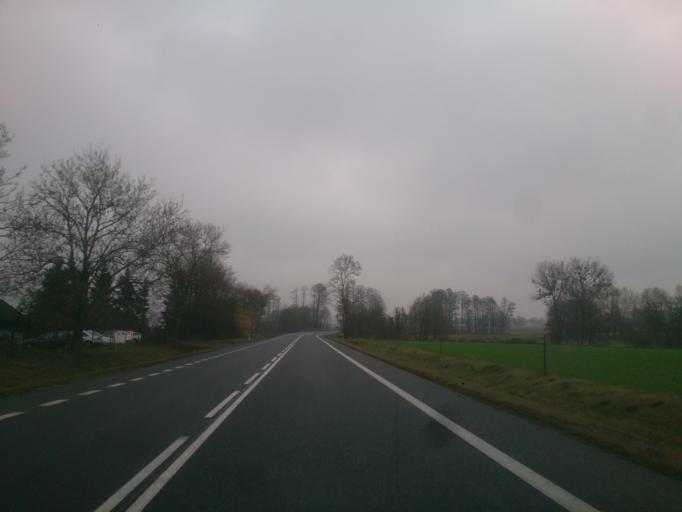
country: PL
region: Masovian Voivodeship
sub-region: Powiat sierpecki
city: Rosciszewo
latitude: 52.8249
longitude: 19.7687
